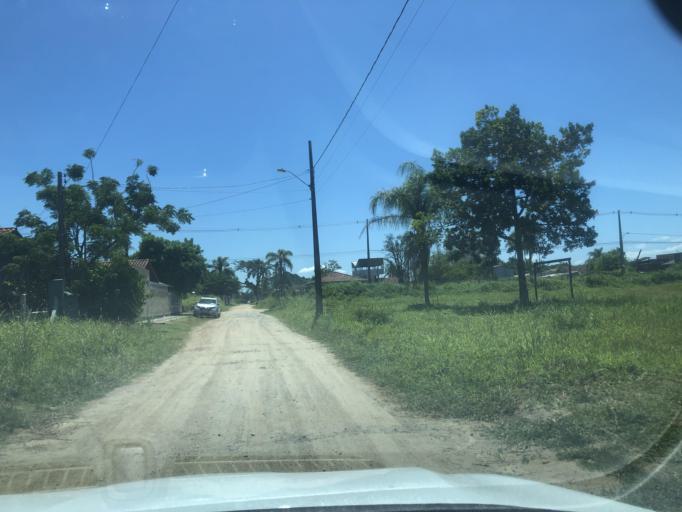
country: BR
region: Santa Catarina
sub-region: Sao Francisco Do Sul
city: Sao Francisco do Sul
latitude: -26.2232
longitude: -48.5270
